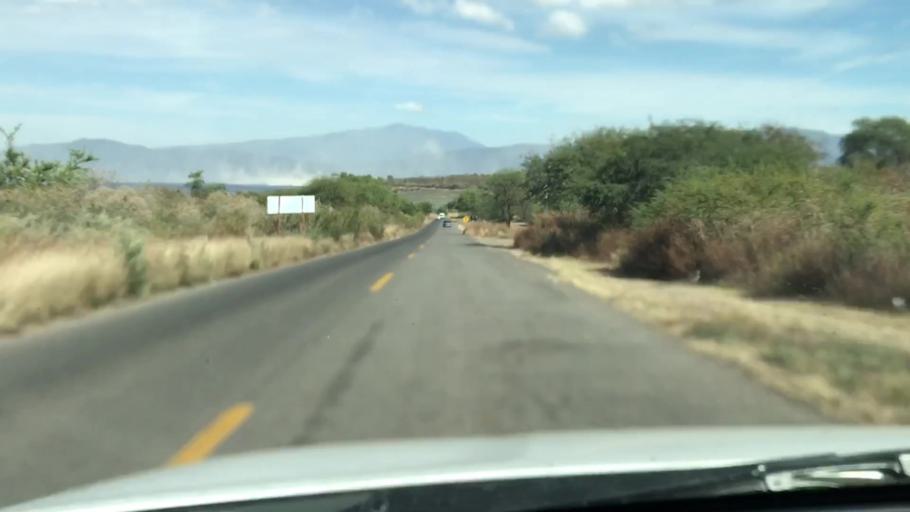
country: MX
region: Jalisco
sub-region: Zacoalco de Torres
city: Barranca de Otates (Barranca de Otatan)
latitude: 20.2577
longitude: -103.6663
